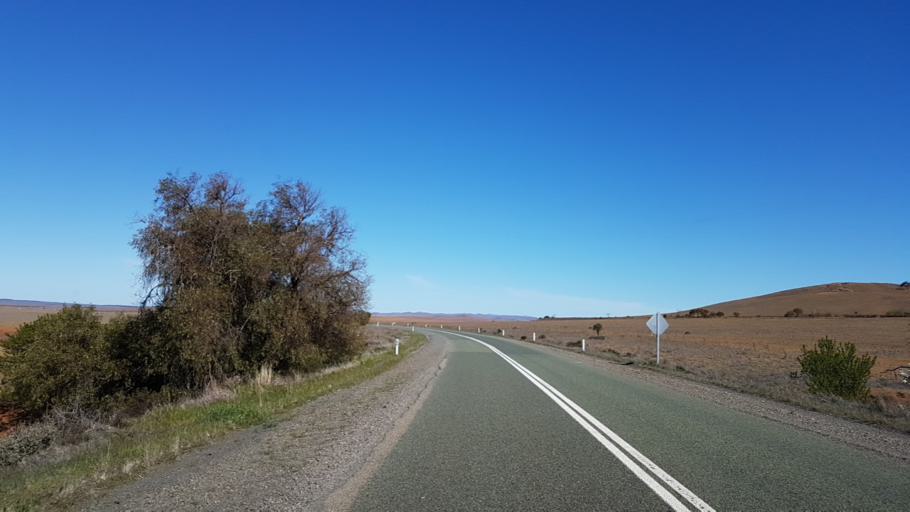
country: AU
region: South Australia
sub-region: Peterborough
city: Peterborough
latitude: -33.0742
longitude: 138.8928
